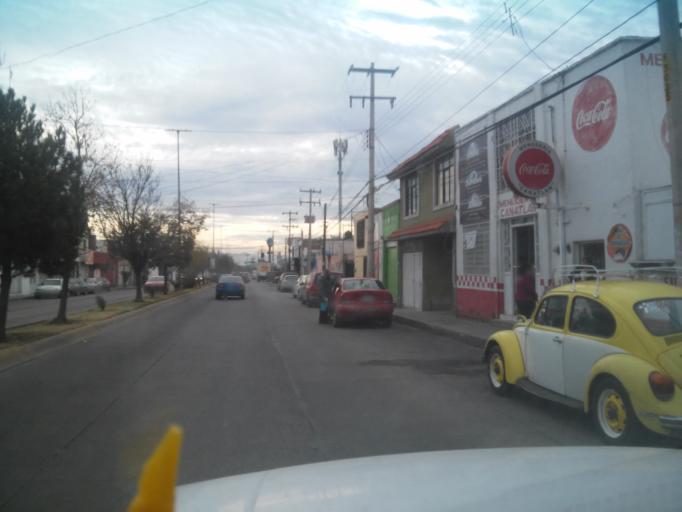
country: MX
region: Durango
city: Victoria de Durango
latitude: 24.0119
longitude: -104.6708
